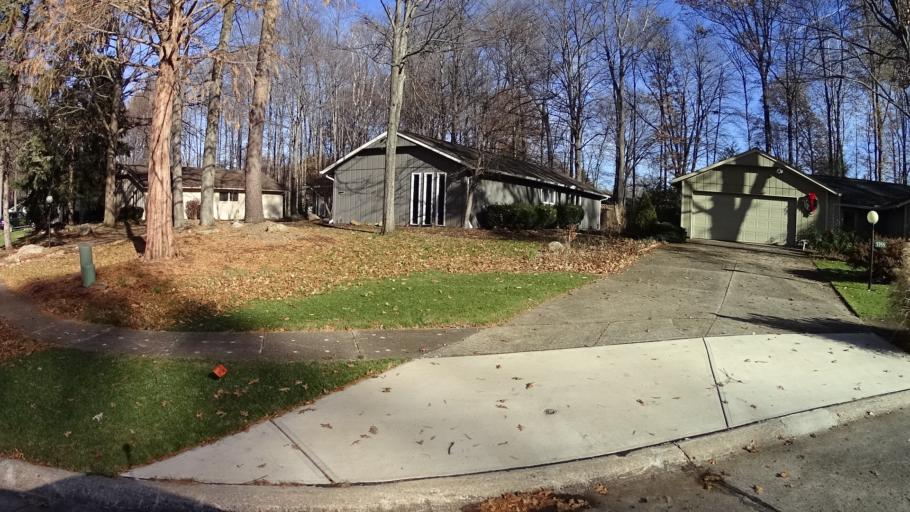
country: US
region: Ohio
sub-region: Lorain County
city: North Ridgeville
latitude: 41.4019
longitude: -81.9756
